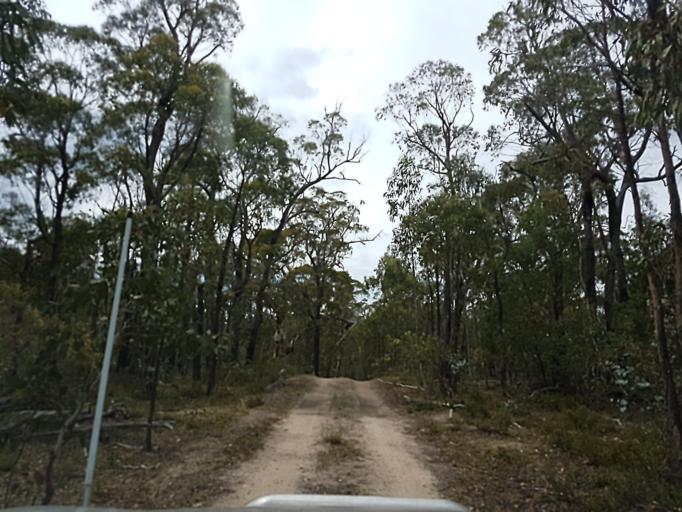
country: AU
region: New South Wales
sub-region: Snowy River
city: Jindabyne
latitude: -36.8347
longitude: 148.2315
